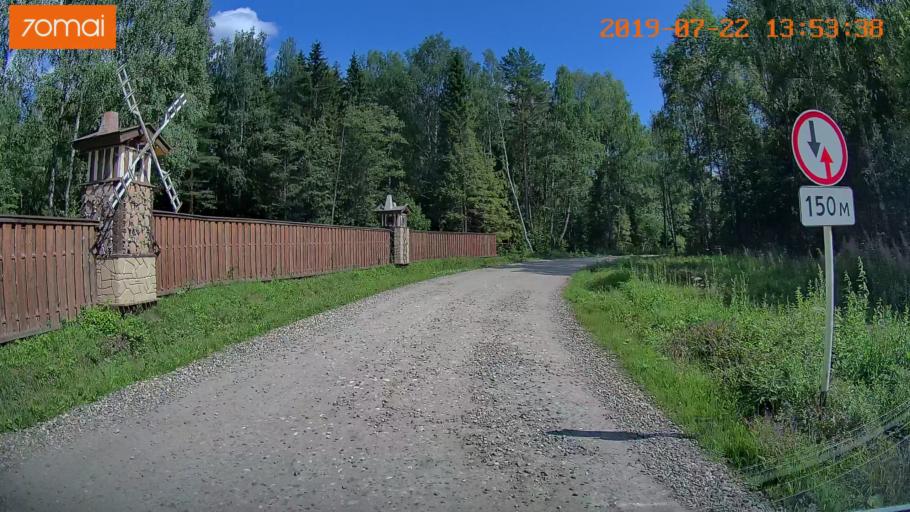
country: RU
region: Ivanovo
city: Novo-Talitsy
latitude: 57.0803
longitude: 40.8774
